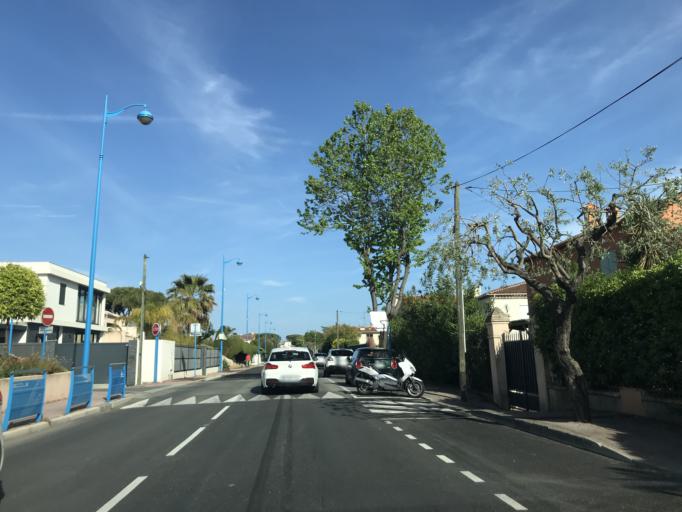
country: FR
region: Provence-Alpes-Cote d'Azur
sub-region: Departement des Alpes-Maritimes
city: Mandelieu-la-Napoule
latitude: 43.5395
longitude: 6.9389
